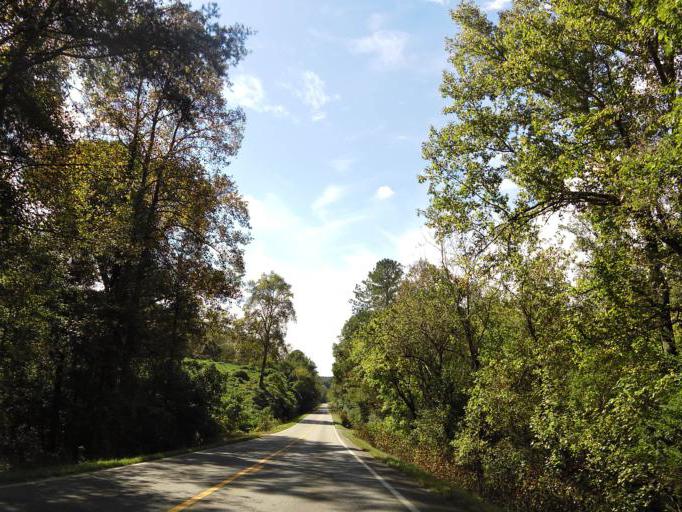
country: US
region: Georgia
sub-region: Pickens County
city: Nelson
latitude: 34.4125
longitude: -84.3915
